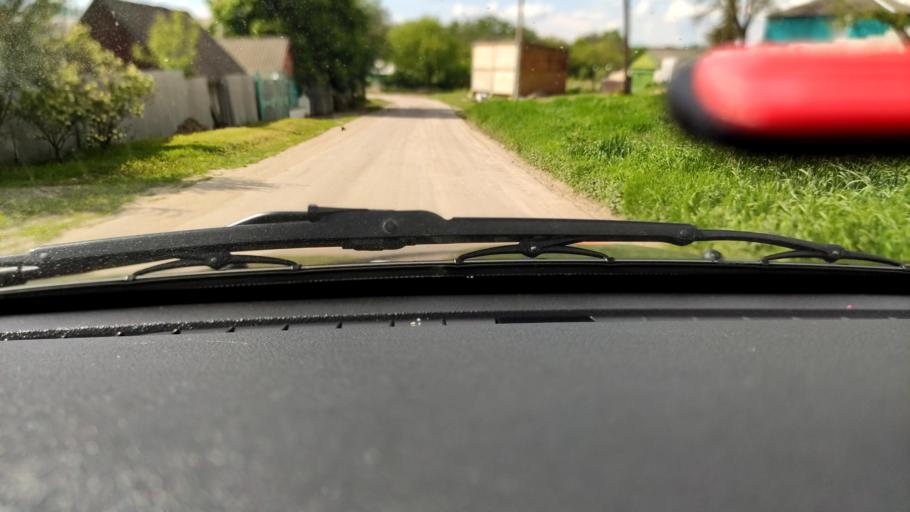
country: RU
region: Voronezj
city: Uryv-Pokrovka
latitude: 51.1099
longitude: 39.1643
